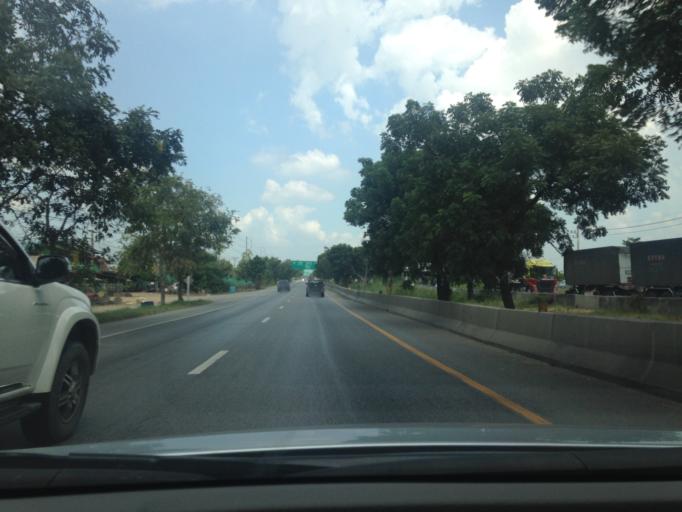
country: TH
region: Pathum Thani
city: Sam Khok
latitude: 14.0851
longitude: 100.5084
